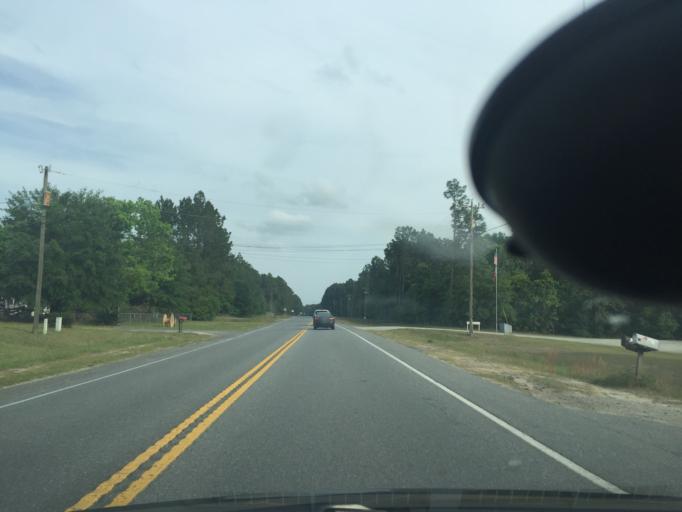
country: US
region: Georgia
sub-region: Chatham County
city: Bloomingdale
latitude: 32.0527
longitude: -81.3430
